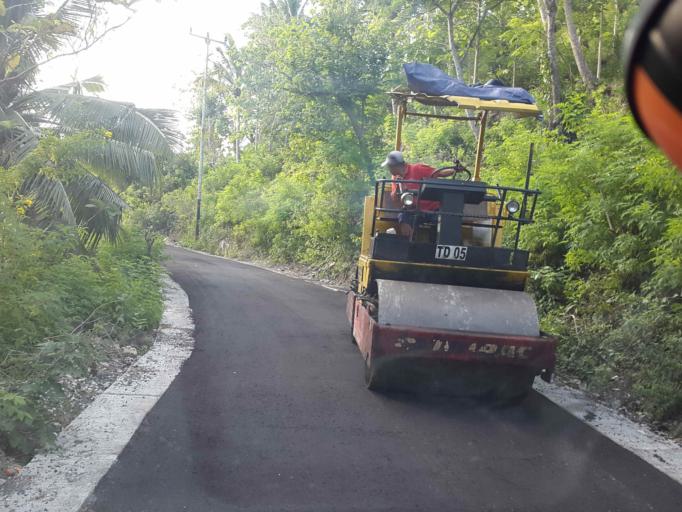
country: ID
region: Bali
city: Pejukutan
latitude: -8.7525
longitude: 115.5911
